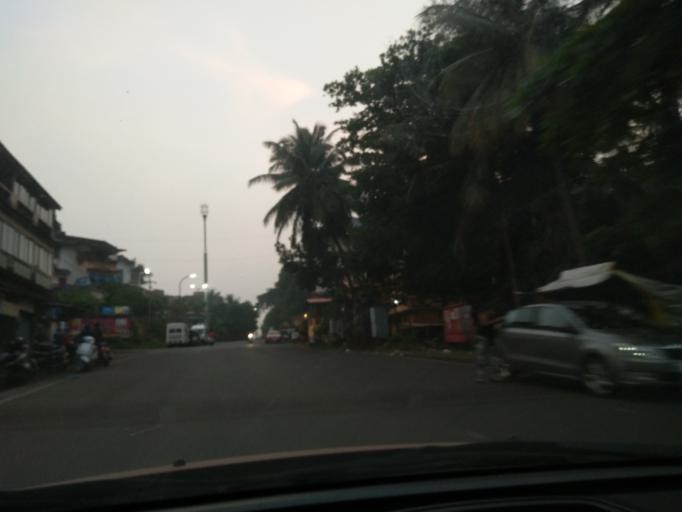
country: IN
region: Goa
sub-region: South Goa
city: Davorlim
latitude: 15.2781
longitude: 73.9759
